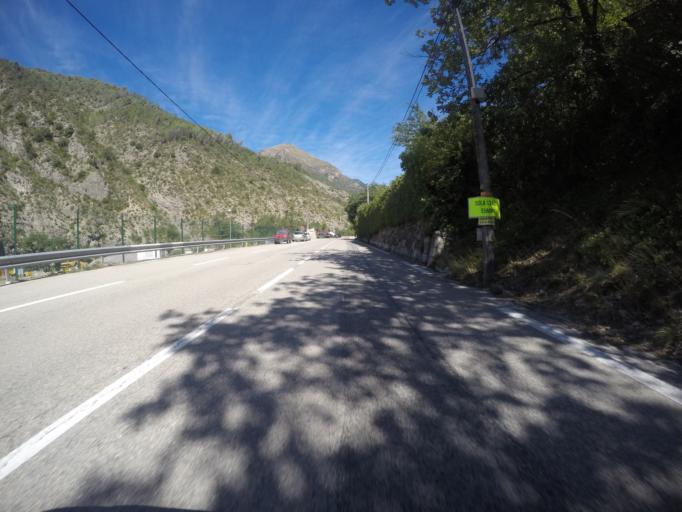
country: FR
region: Provence-Alpes-Cote d'Azur
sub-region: Departement des Alpes-Maritimes
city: Gilette
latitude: 43.9464
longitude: 7.1615
